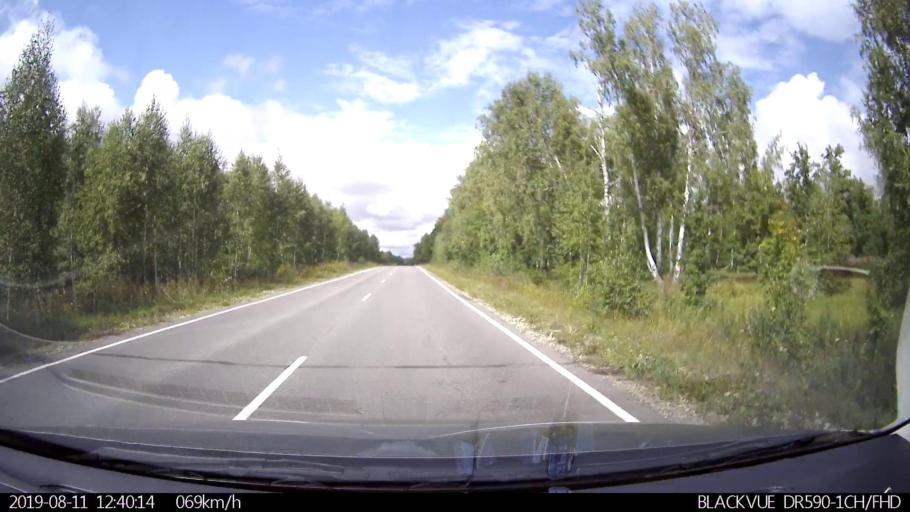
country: RU
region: Ulyanovsk
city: Ignatovka
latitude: 53.8375
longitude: 47.7840
